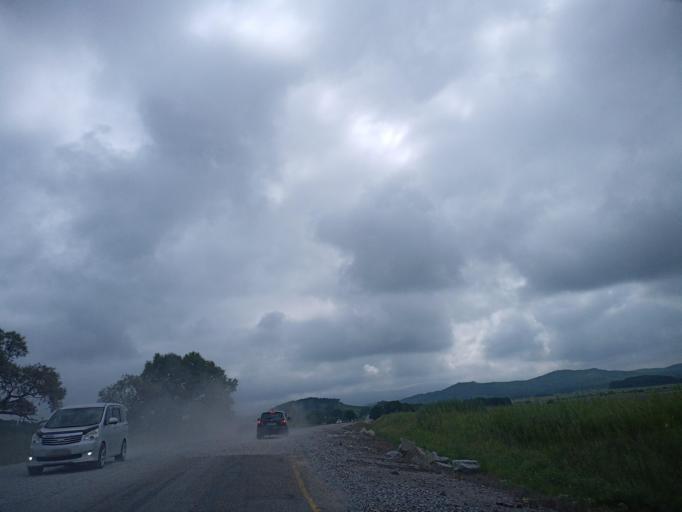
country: RU
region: Primorskiy
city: Dal'nerechensk
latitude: 46.0378
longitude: 133.8688
